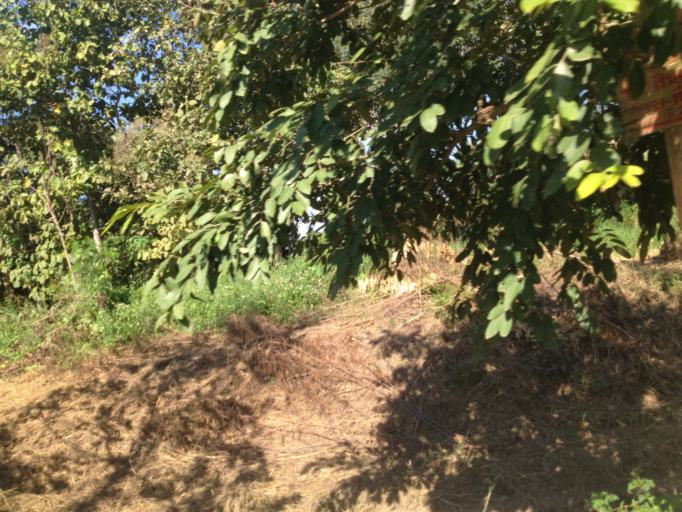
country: TH
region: Chiang Mai
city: Hang Dong
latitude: 18.6843
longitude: 98.9728
